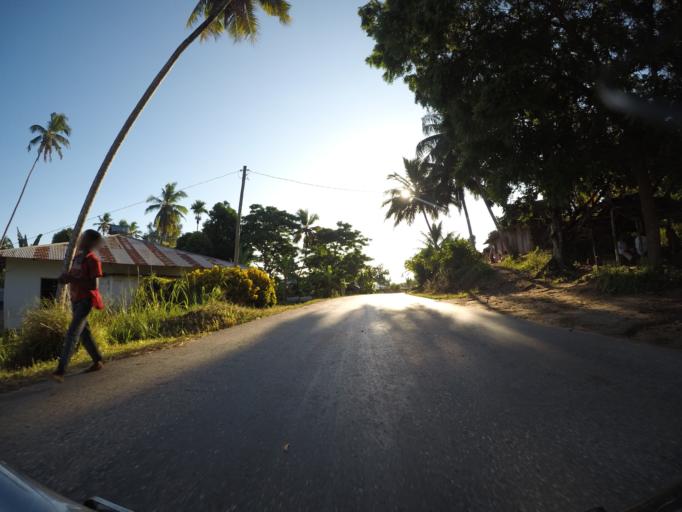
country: TZ
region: Pemba South
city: Mtambile
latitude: -5.3791
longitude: 39.6860
